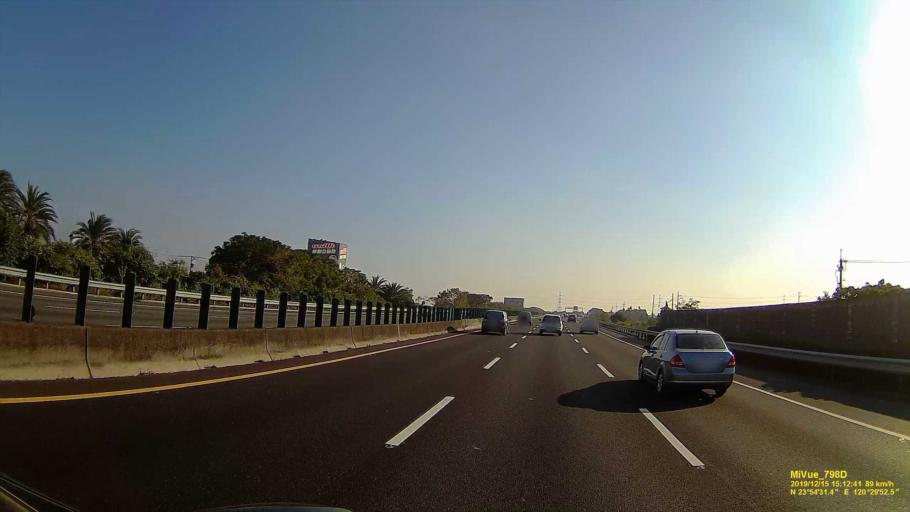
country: TW
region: Taiwan
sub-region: Nantou
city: Nantou
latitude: 23.9085
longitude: 120.4979
